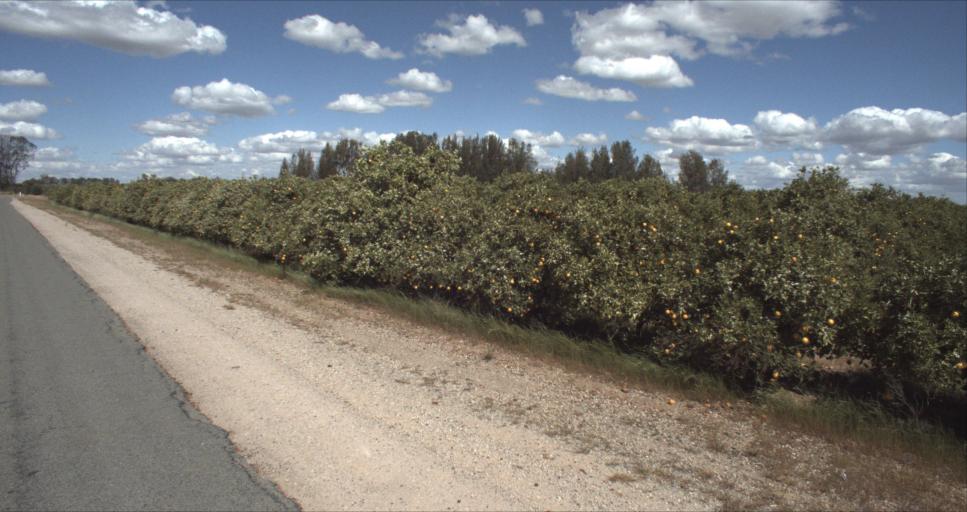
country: AU
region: New South Wales
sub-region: Leeton
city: Leeton
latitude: -34.5099
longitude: 146.2260
